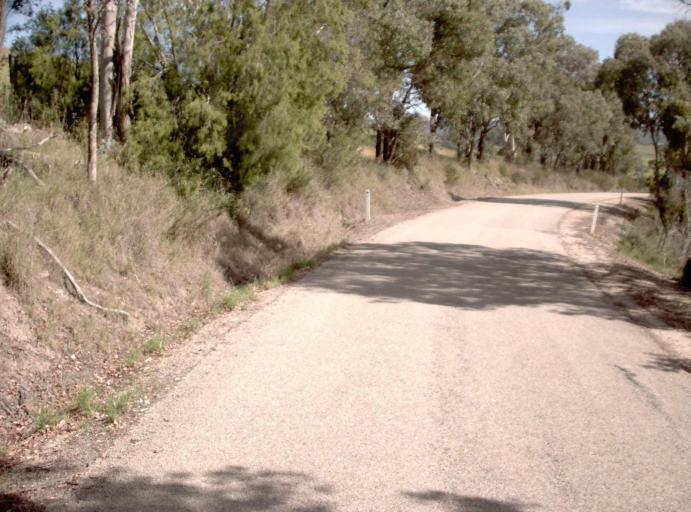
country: AU
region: Victoria
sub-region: East Gippsland
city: Lakes Entrance
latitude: -37.5129
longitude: 148.1419
